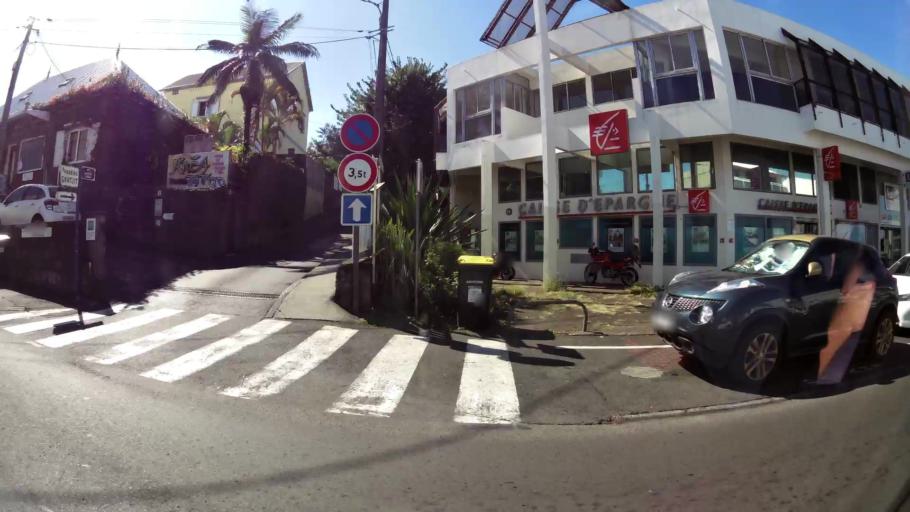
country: RE
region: Reunion
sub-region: Reunion
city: Le Tampon
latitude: -21.2774
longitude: 55.5142
